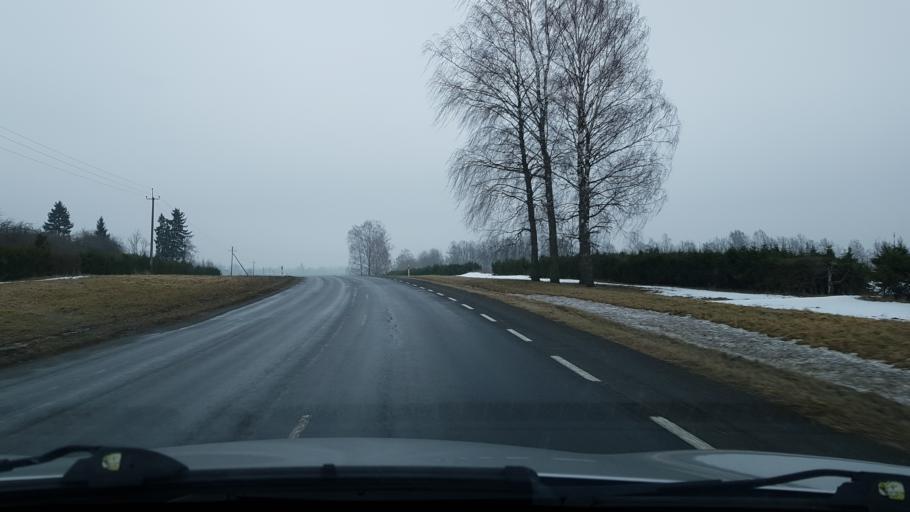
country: EE
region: Viljandimaa
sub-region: Viiratsi vald
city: Viiratsi
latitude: 58.2507
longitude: 25.8296
